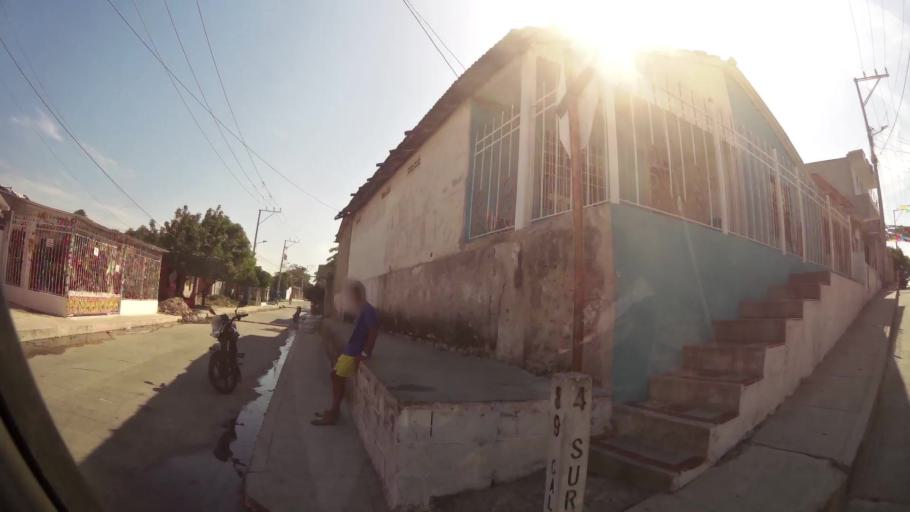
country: CO
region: Atlantico
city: Barranquilla
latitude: 10.9326
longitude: -74.8236
